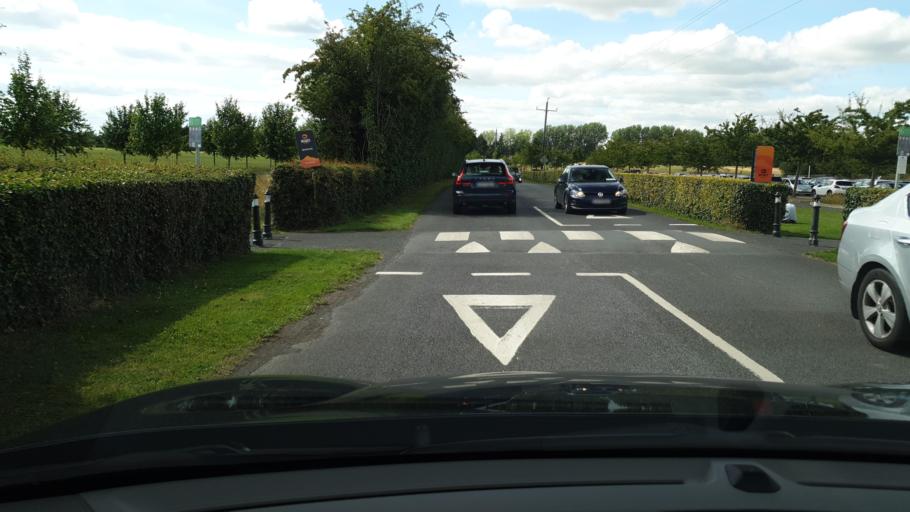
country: IE
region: Leinster
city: Lucan
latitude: 53.3668
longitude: -6.4642
